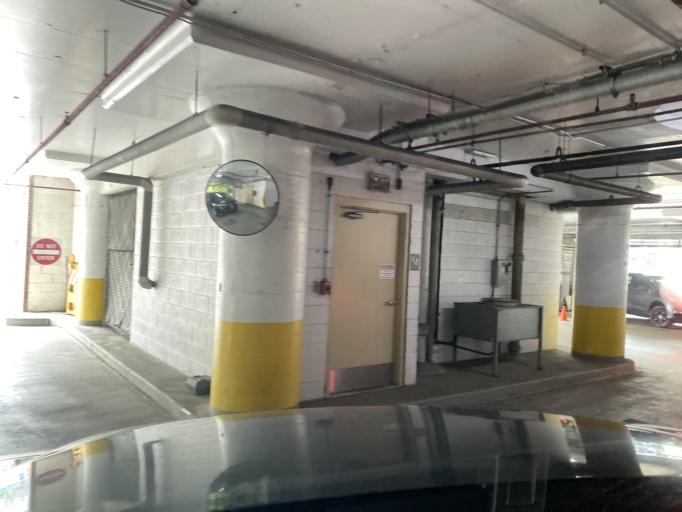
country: US
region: Massachusetts
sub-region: Norfolk County
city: Brookline
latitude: 42.3461
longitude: -71.1024
